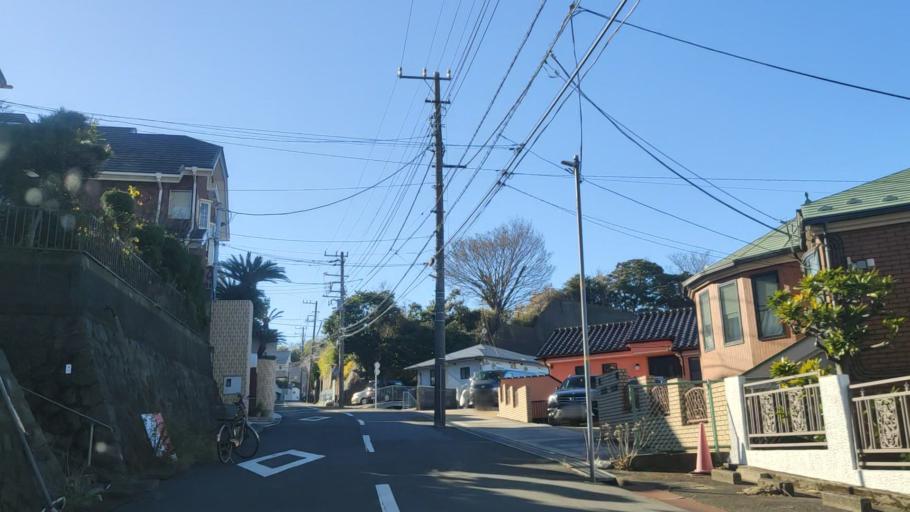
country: JP
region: Kanagawa
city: Yokohama
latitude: 35.4210
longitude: 139.6599
